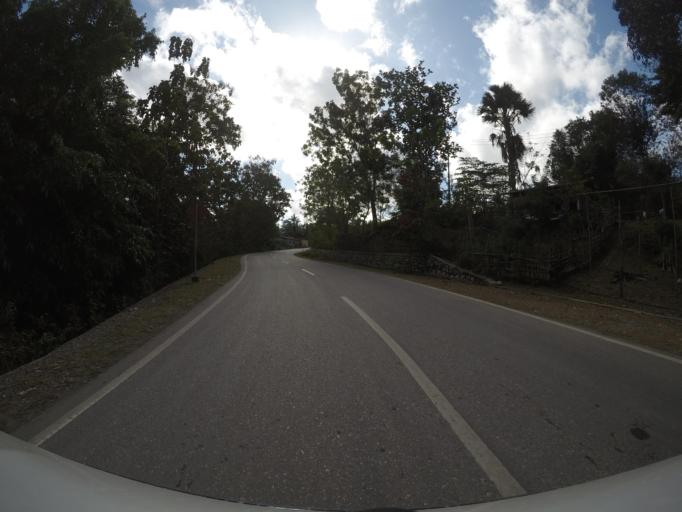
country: TL
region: Viqueque
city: Viqueque
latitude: -8.8731
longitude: 126.3751
